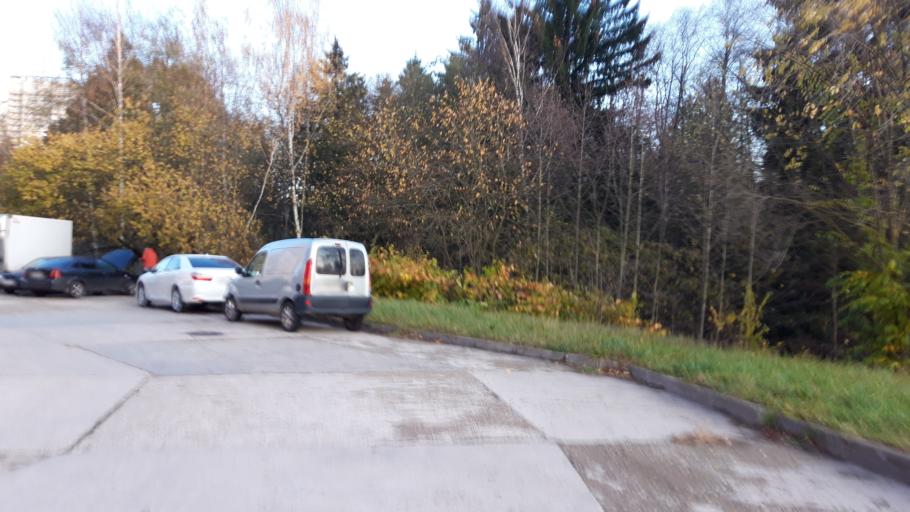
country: RU
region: Moscow
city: Zelenograd
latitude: 55.9917
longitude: 37.1877
